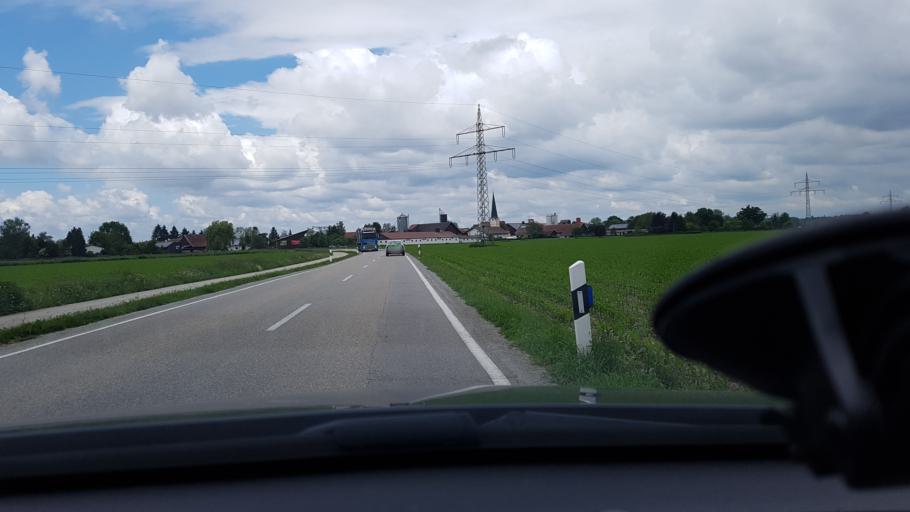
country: DE
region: Bavaria
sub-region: Lower Bavaria
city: Pocking
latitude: 48.4064
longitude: 13.3531
